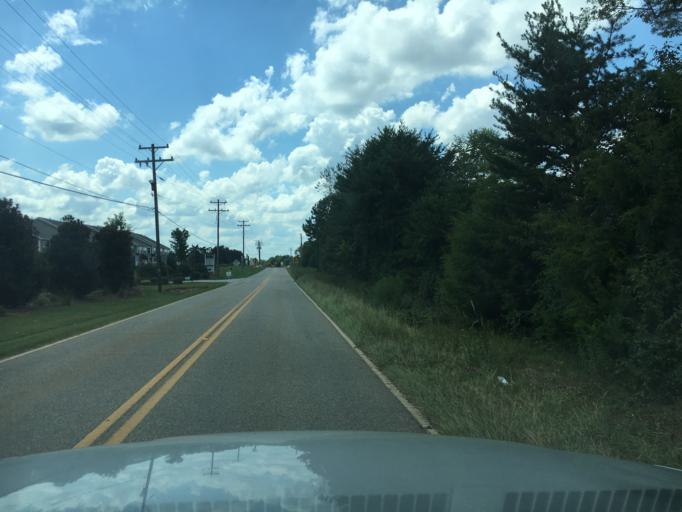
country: US
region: South Carolina
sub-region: Spartanburg County
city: Wellford
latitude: 34.8908
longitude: -82.0686
